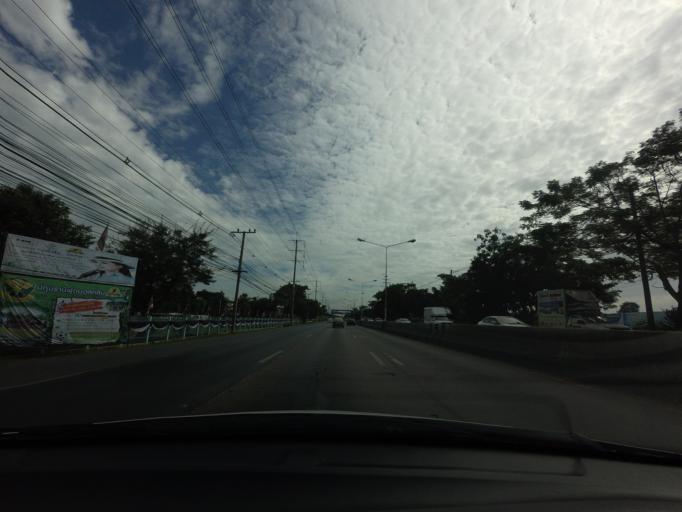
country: TH
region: Pathum Thani
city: Thanyaburi
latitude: 14.0146
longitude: 100.7209
